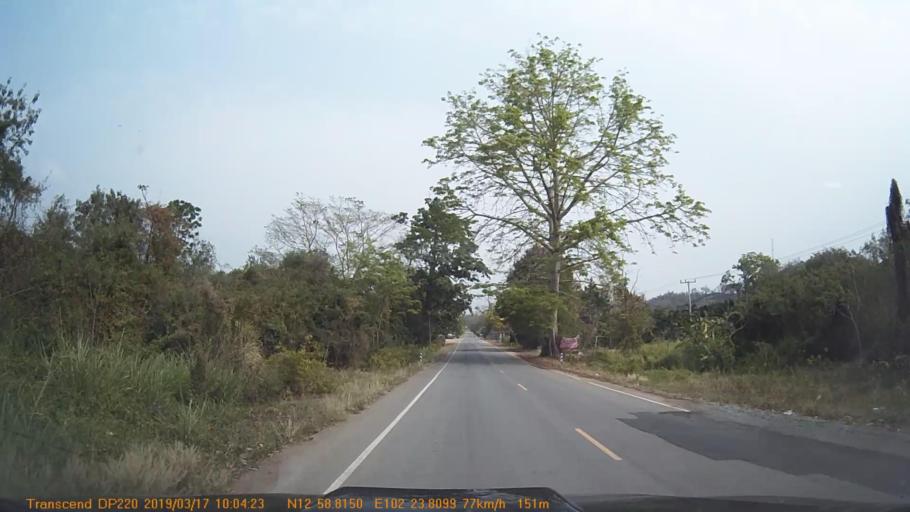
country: TH
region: Chanthaburi
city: Pong Nam Ron
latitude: 12.9824
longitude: 102.3969
